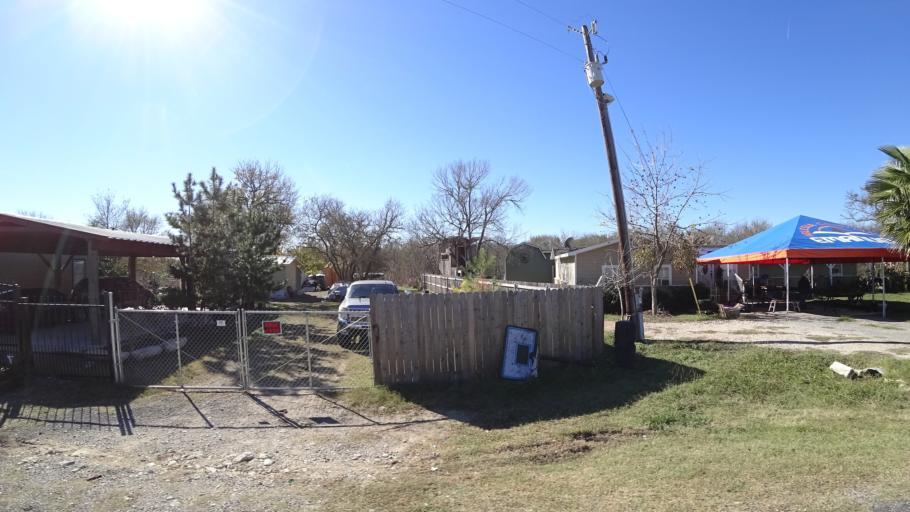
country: US
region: Texas
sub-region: Travis County
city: Garfield
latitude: 30.1275
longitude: -97.6151
